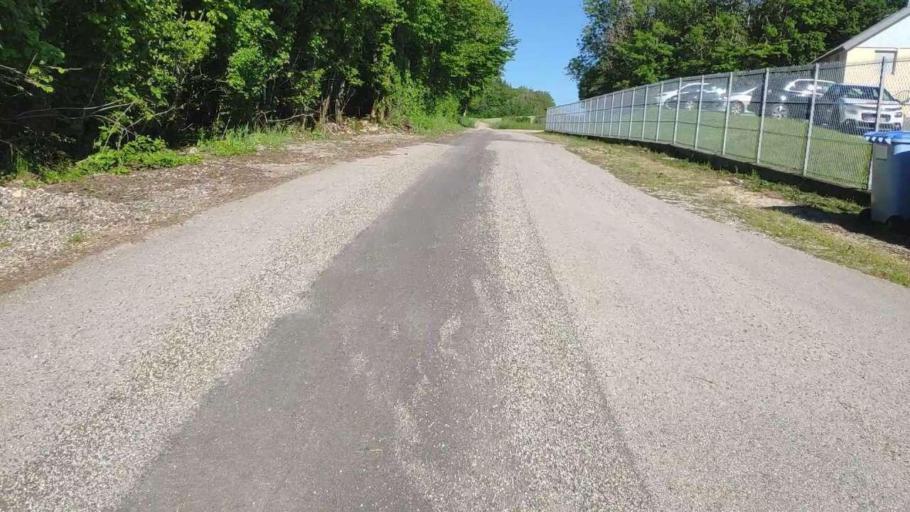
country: FR
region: Franche-Comte
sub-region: Departement du Jura
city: Perrigny
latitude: 46.6851
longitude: 5.6293
